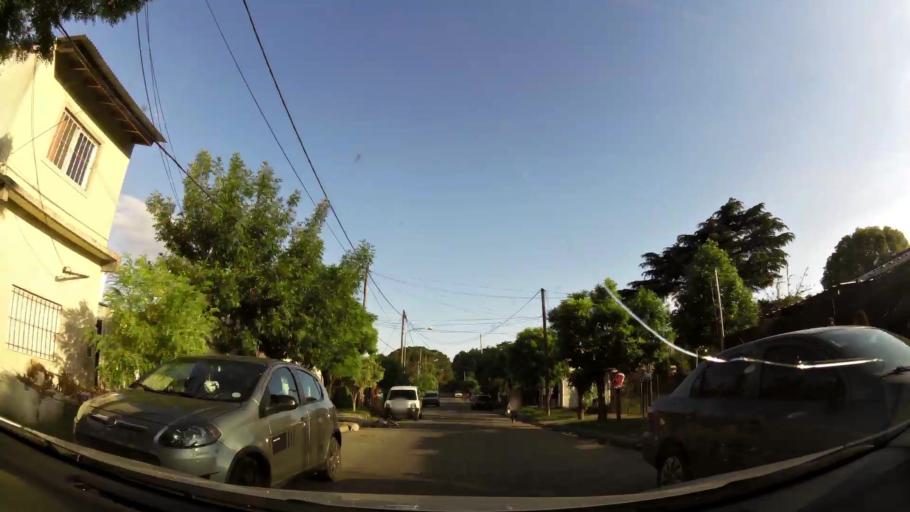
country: AR
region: Buenos Aires
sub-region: Partido de Tigre
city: Tigre
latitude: -34.4522
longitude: -58.6297
